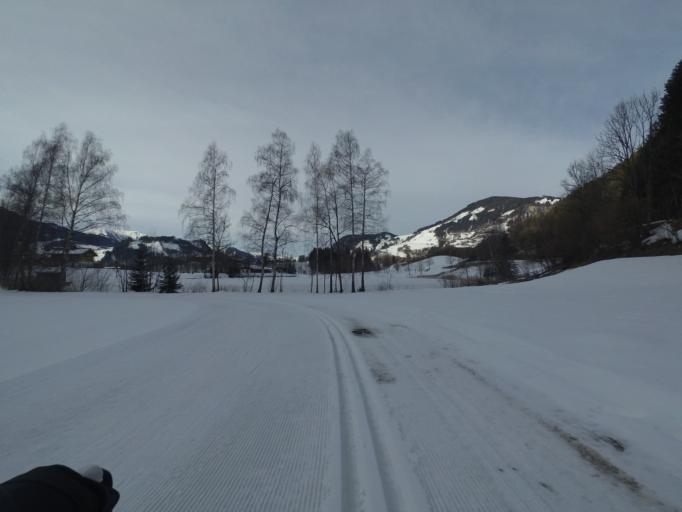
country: AT
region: Salzburg
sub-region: Politischer Bezirk Zell am See
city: Lend
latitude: 47.3148
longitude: 13.0444
